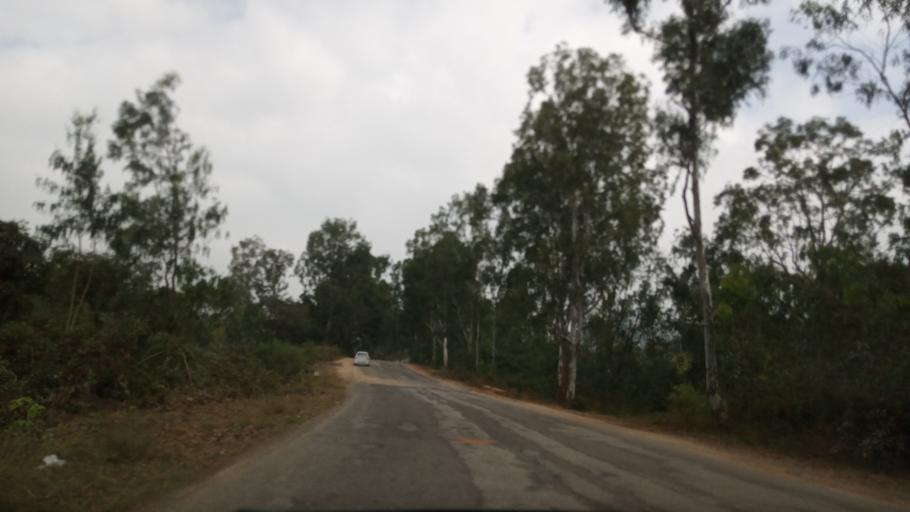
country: IN
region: Andhra Pradesh
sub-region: Chittoor
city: Madanapalle
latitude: 13.5067
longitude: 78.3351
